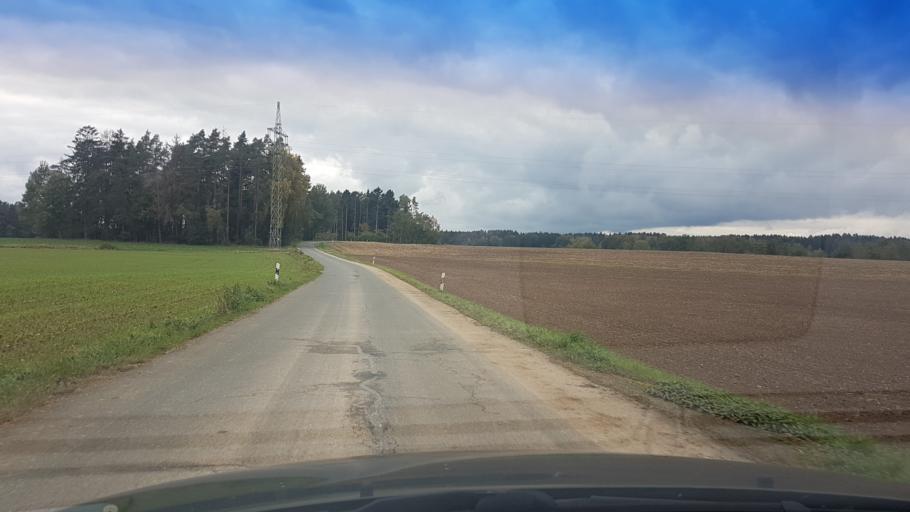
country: DE
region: Bavaria
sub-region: Upper Franconia
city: Stadelhofen
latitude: 50.0132
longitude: 11.2538
